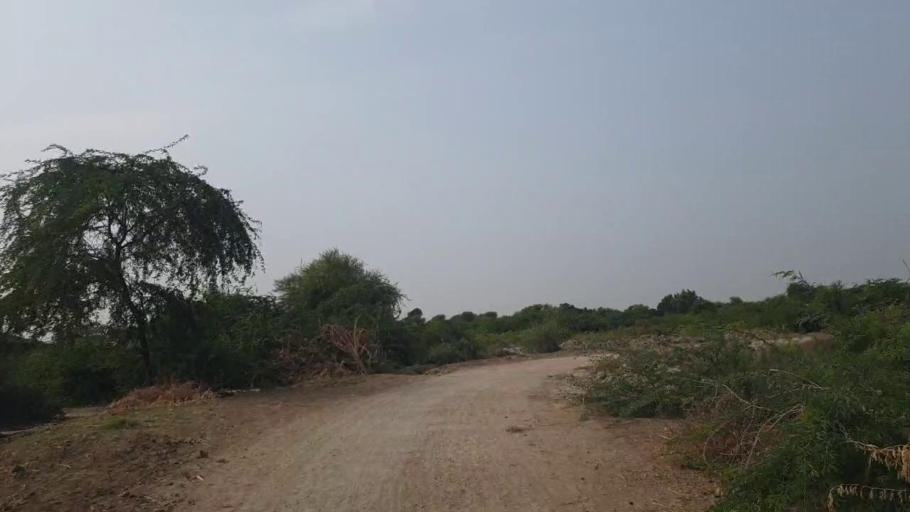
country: PK
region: Sindh
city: Badin
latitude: 24.5889
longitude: 68.7404
